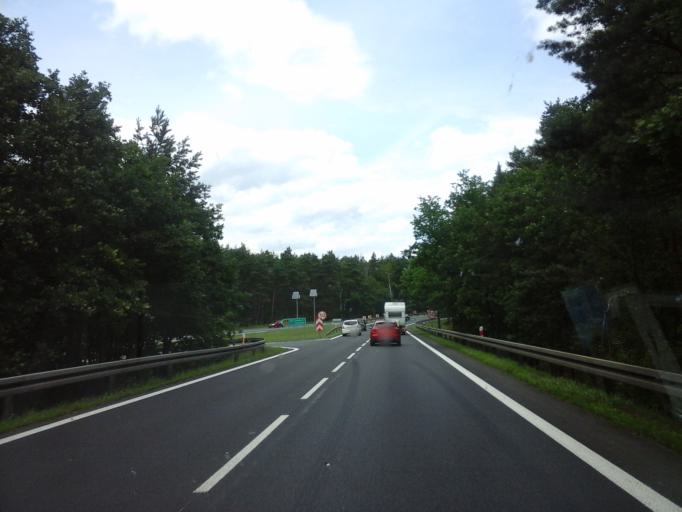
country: PL
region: West Pomeranian Voivodeship
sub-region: Powiat stargardzki
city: Kobylanka
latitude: 53.4259
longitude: 14.7722
